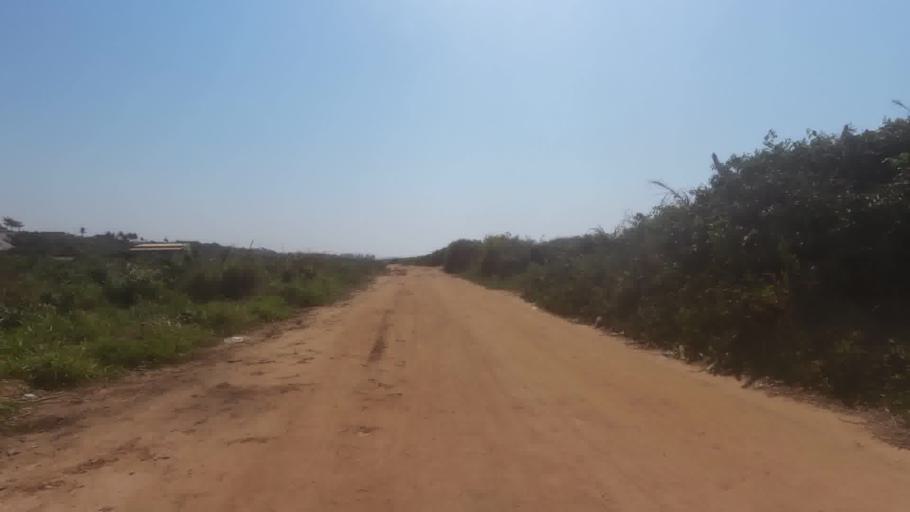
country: BR
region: Espirito Santo
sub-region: Marataizes
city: Marataizes
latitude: -21.0879
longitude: -40.8427
